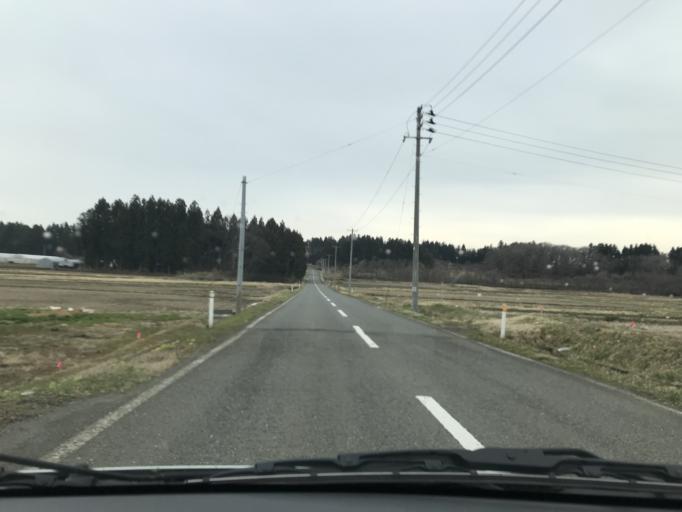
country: JP
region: Iwate
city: Mizusawa
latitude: 39.0960
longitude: 141.0691
